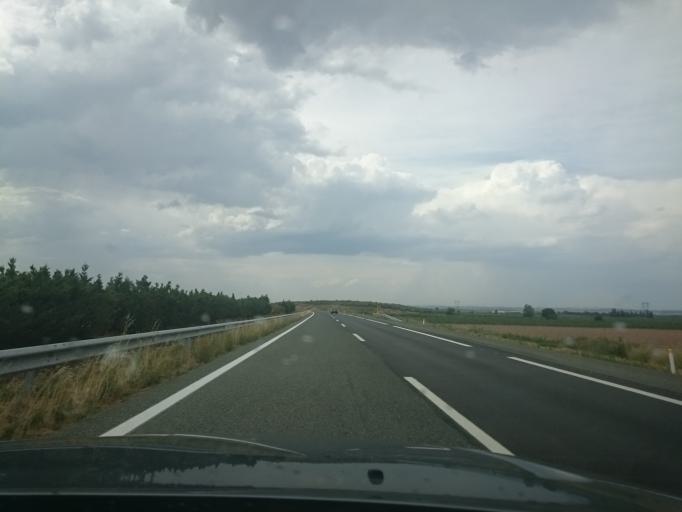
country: ES
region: Navarre
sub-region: Provincia de Navarra
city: Corella
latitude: 42.1427
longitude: -1.7829
